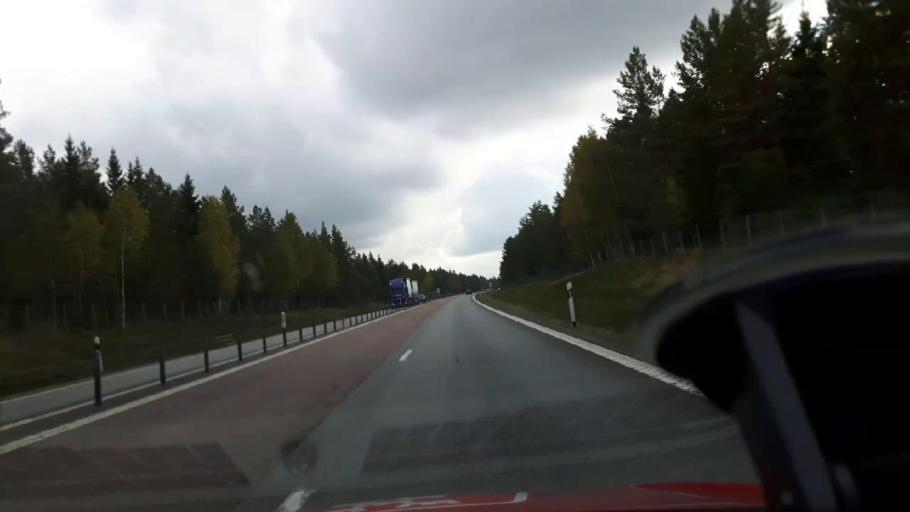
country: SE
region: Gaevleborg
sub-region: Gavle Kommun
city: Norrsundet
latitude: 60.8310
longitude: 17.0820
